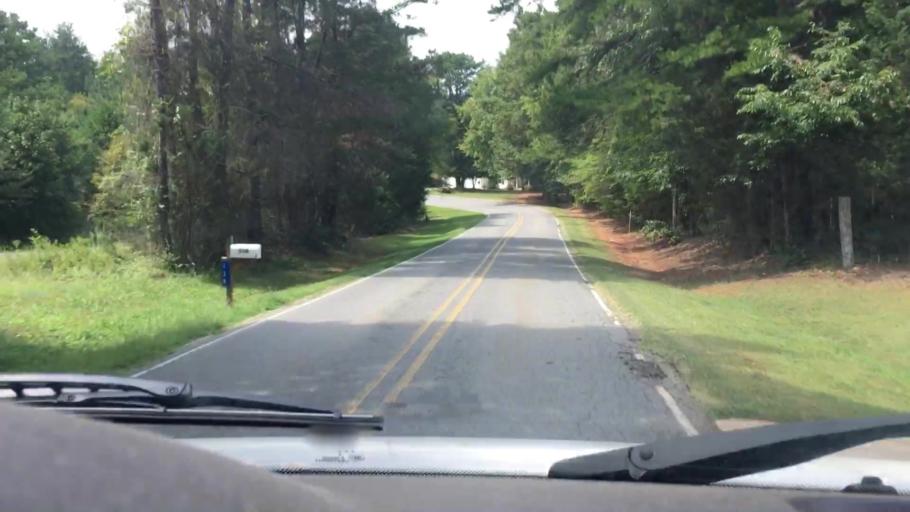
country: US
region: North Carolina
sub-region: Gaston County
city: Davidson
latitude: 35.5076
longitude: -80.7997
